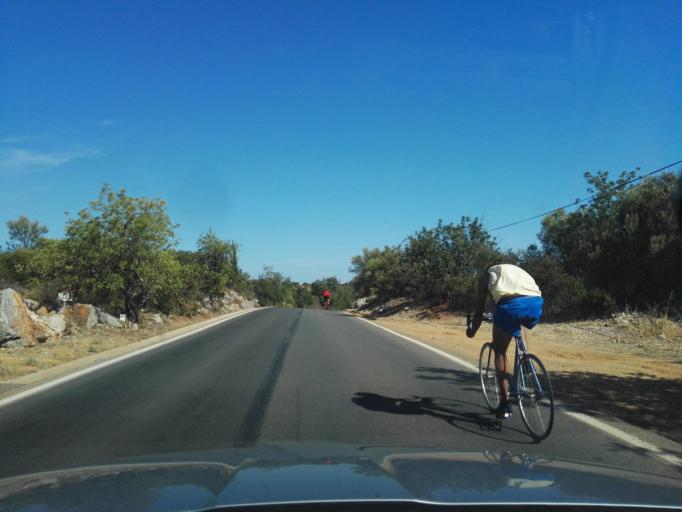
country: PT
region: Faro
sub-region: Tavira
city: Luz
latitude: 37.1385
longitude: -7.7052
